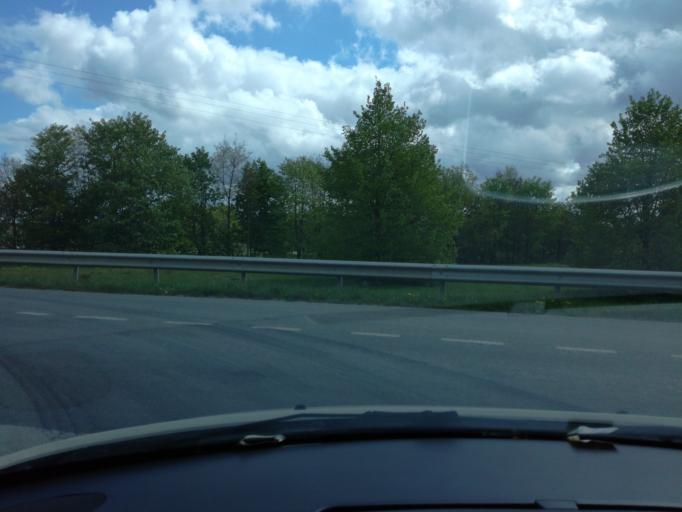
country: FR
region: Picardie
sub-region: Departement de la Somme
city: Vignacourt
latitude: 49.9926
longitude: 2.1778
